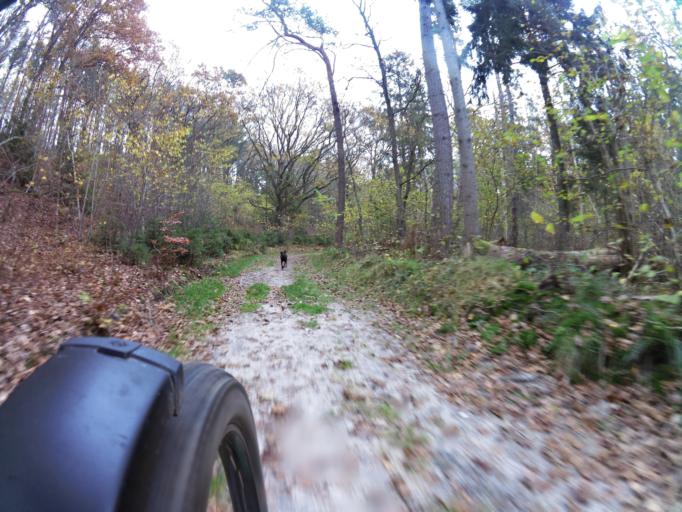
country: PL
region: Pomeranian Voivodeship
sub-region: Powiat pucki
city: Krokowa
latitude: 54.8308
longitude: 18.1123
